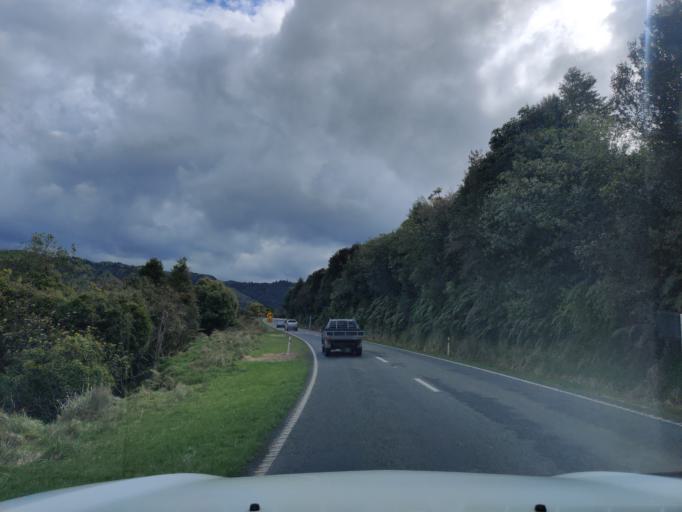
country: NZ
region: Manawatu-Wanganui
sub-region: Ruapehu District
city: Waiouru
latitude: -39.5055
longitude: 175.2936
